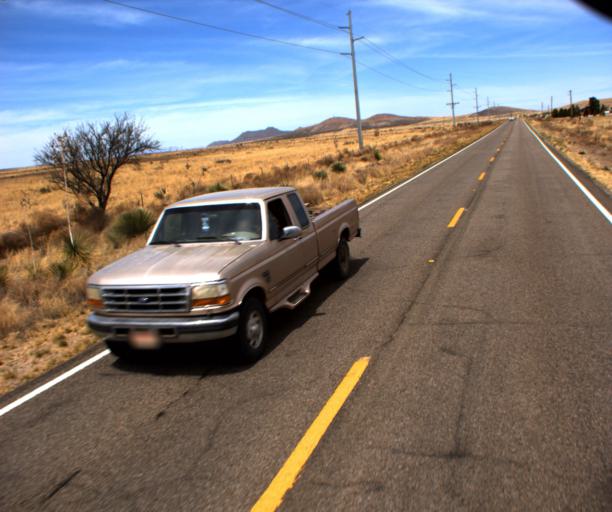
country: US
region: Arizona
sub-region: Cochise County
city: Tombstone
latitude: 31.8694
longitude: -109.6952
